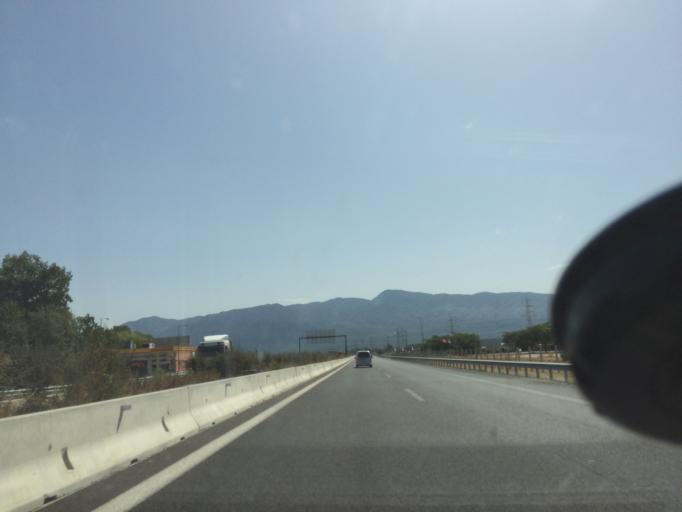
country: GR
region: Central Greece
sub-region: Nomos Fthiotidos
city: Anthili
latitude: 38.8642
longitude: 22.4607
